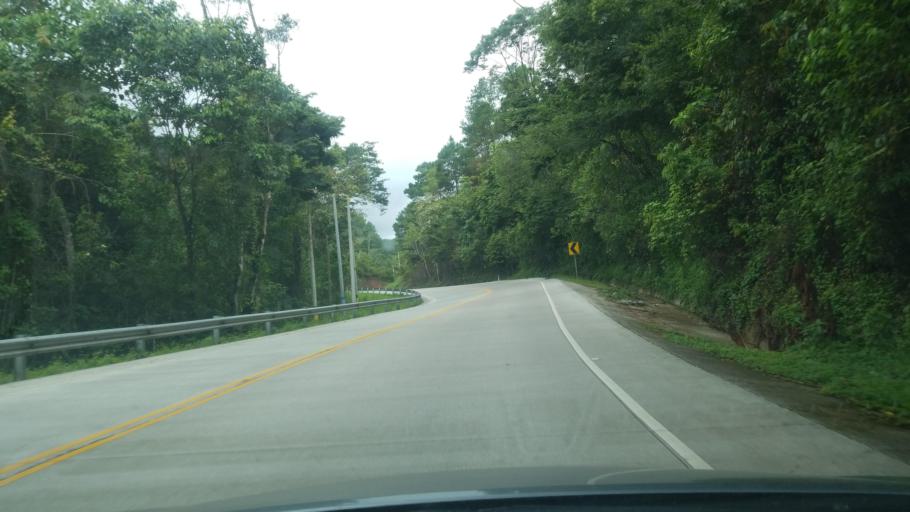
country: HN
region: Copan
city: San Jeronimo
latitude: 14.9317
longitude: -88.9440
